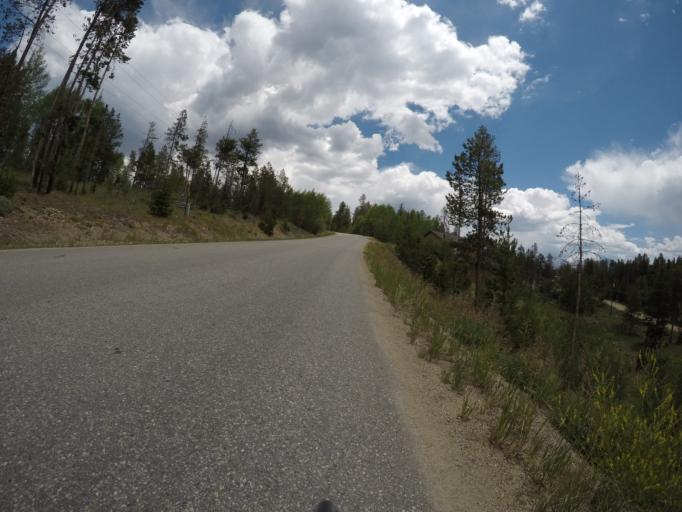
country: US
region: Colorado
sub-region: Grand County
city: Fraser
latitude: 39.9521
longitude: -105.8062
